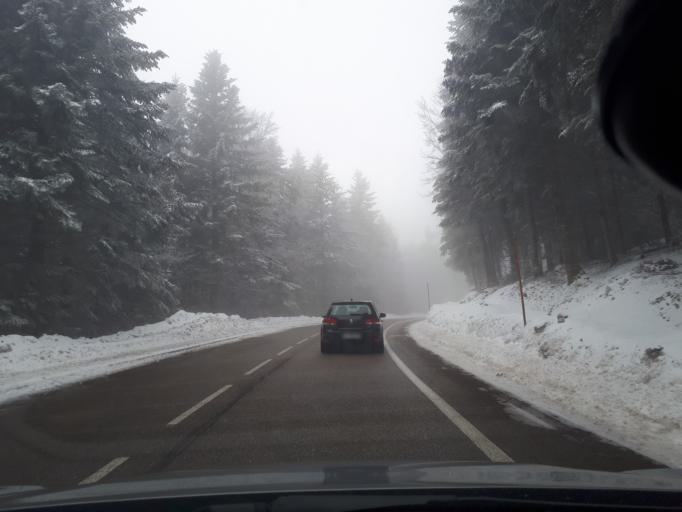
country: FR
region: Rhone-Alpes
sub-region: Departement de l'Isere
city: Vaulnaveys-le-Bas
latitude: 45.0910
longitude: 5.8547
